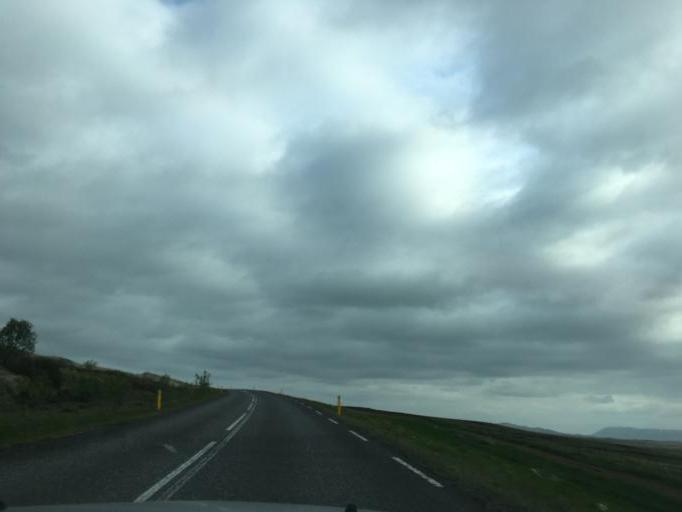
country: IS
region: South
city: Vestmannaeyjar
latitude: 64.1790
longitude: -20.2858
